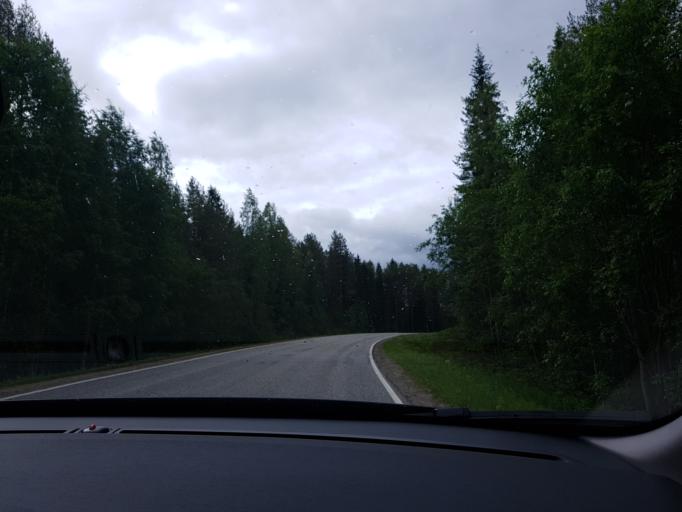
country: FI
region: Kainuu
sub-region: Kehys-Kainuu
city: Kuhmo
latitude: 64.1647
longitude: 29.4689
